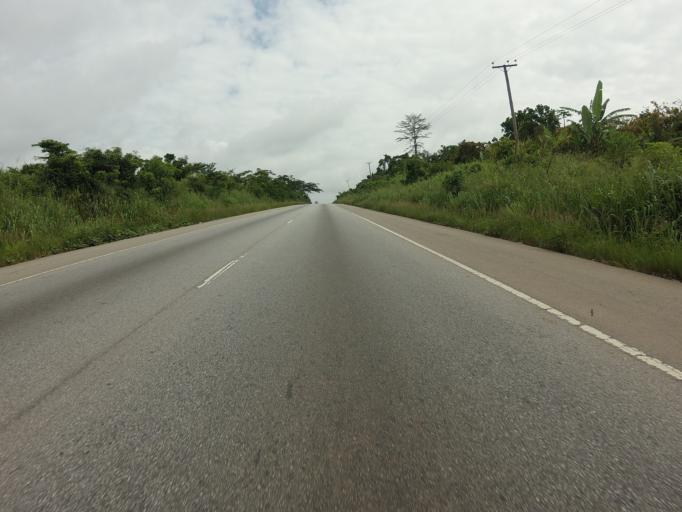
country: GH
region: Ashanti
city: Tafo
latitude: 6.9893
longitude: -1.6917
